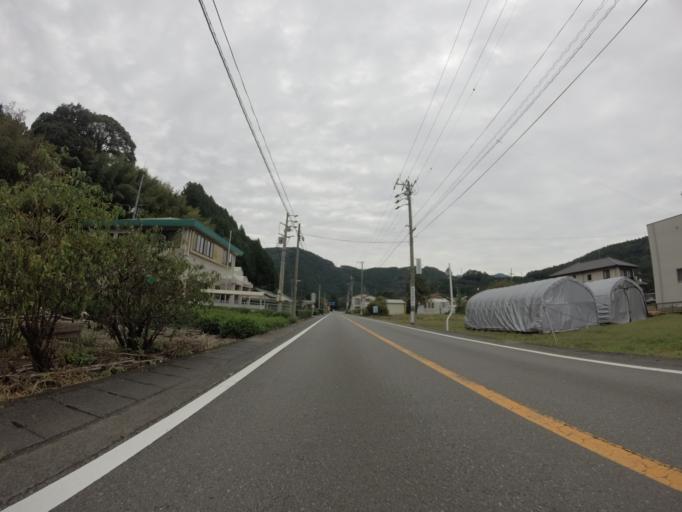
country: JP
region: Shizuoka
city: Kanaya
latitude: 35.0845
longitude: 138.1049
